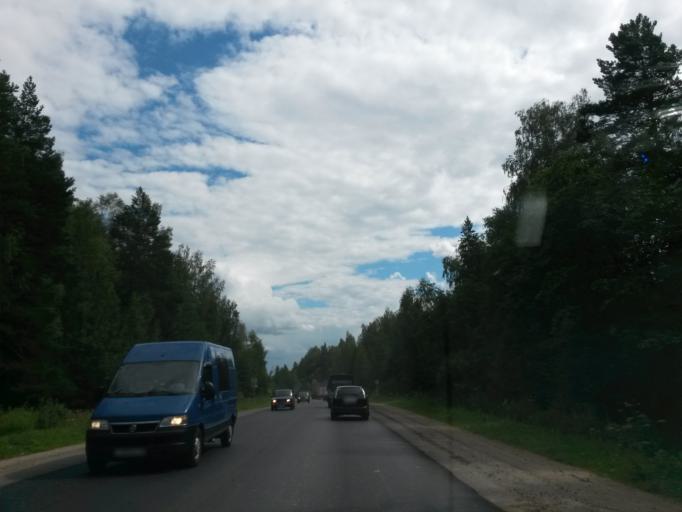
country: RU
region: Ivanovo
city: Novo-Talitsy
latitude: 57.0174
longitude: 40.7823
